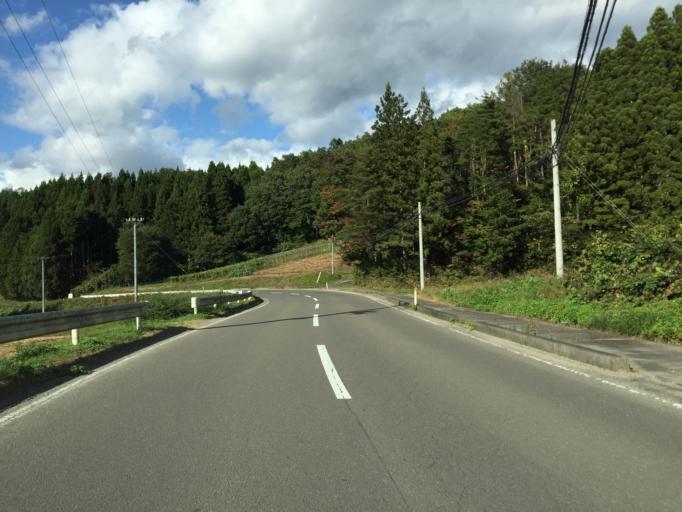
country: JP
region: Miyagi
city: Marumori
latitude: 37.8581
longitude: 140.8299
